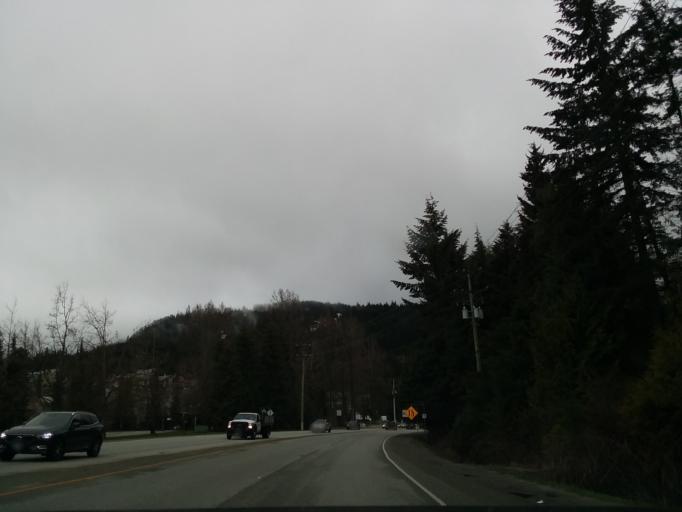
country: CA
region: British Columbia
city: Whistler
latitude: 50.1155
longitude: -122.9594
